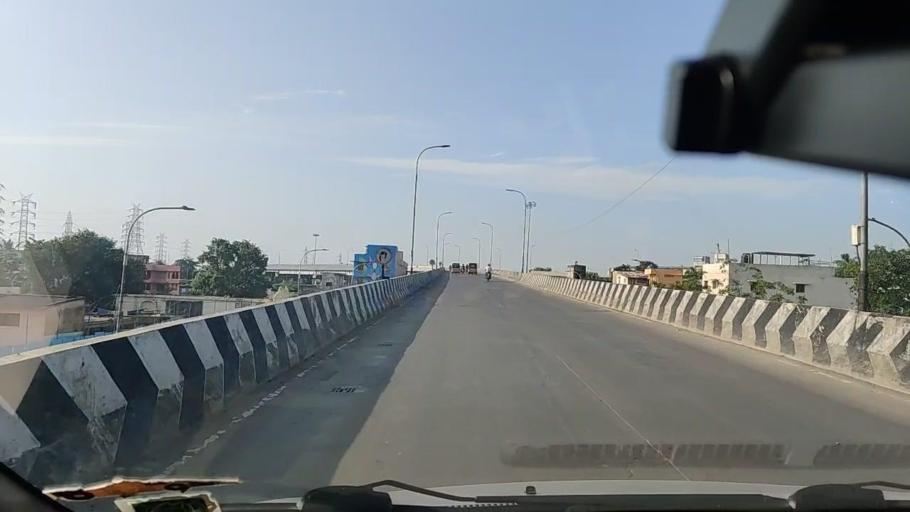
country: IN
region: Tamil Nadu
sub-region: Chennai
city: George Town
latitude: 13.1128
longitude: 80.2655
